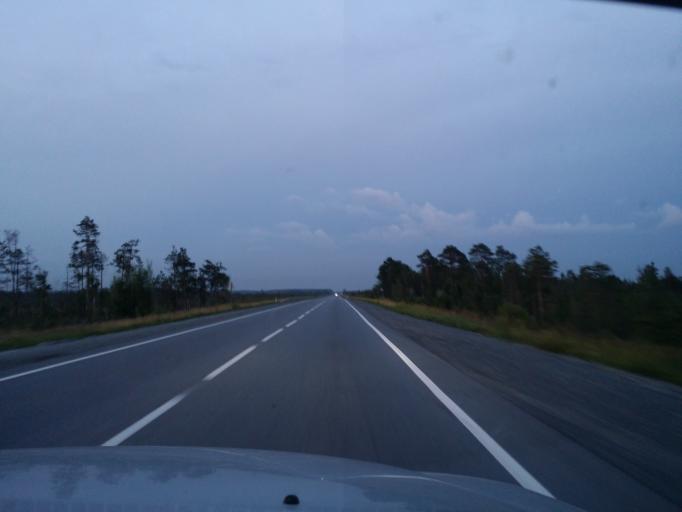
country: RU
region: Khanty-Mansiyskiy Avtonomnyy Okrug
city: Poykovskiy
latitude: 61.3570
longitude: 73.3267
